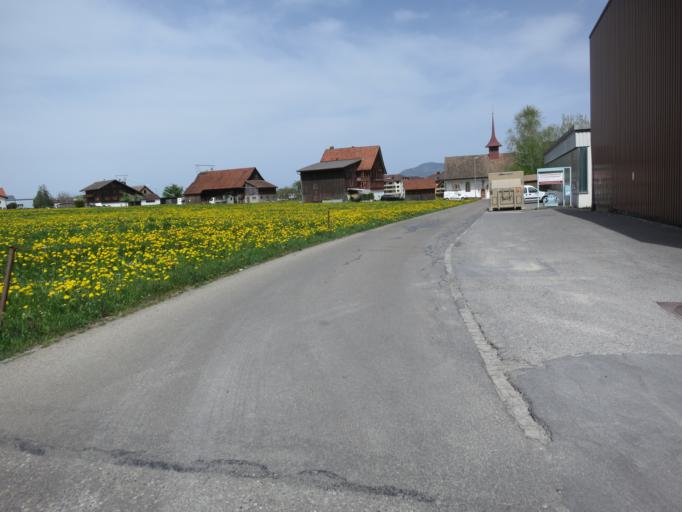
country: CH
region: Schwyz
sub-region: Bezirk March
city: Lachen
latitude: 47.1774
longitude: 8.8735
